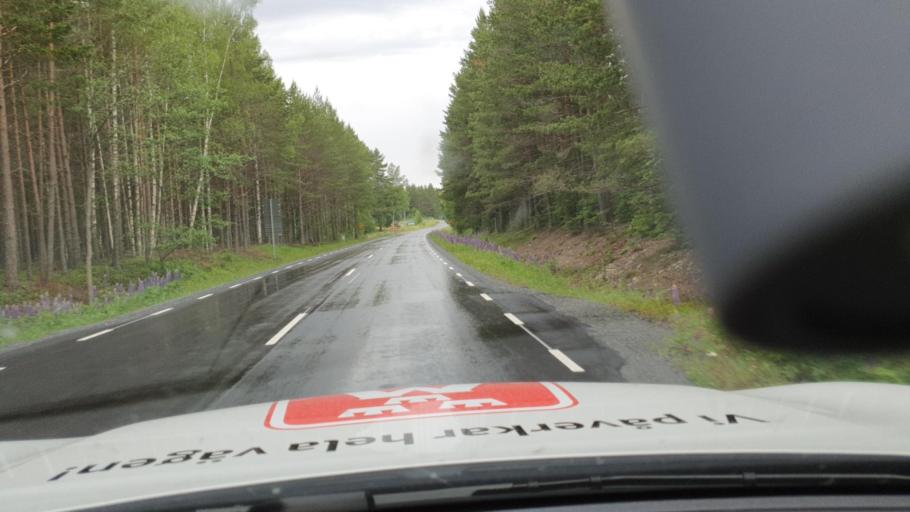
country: SE
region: Vaestra Goetaland
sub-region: Gullspangs Kommun
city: Anderstorp
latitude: 58.9253
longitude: 14.4218
